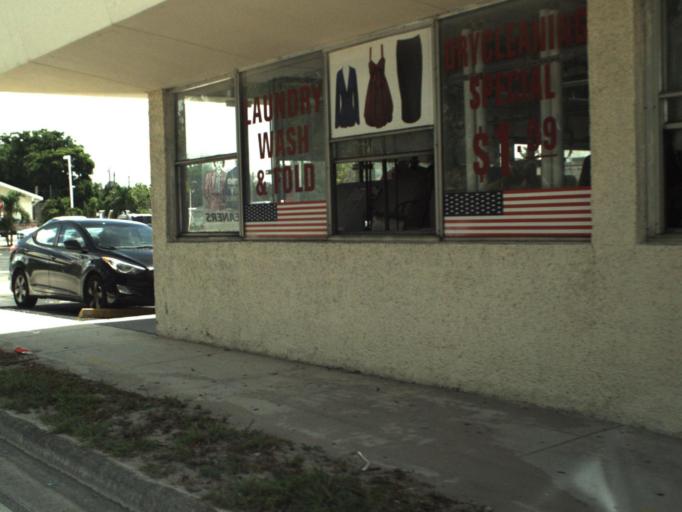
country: US
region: Florida
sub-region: Broward County
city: Pembroke Pines
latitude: 26.0184
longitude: -80.2486
